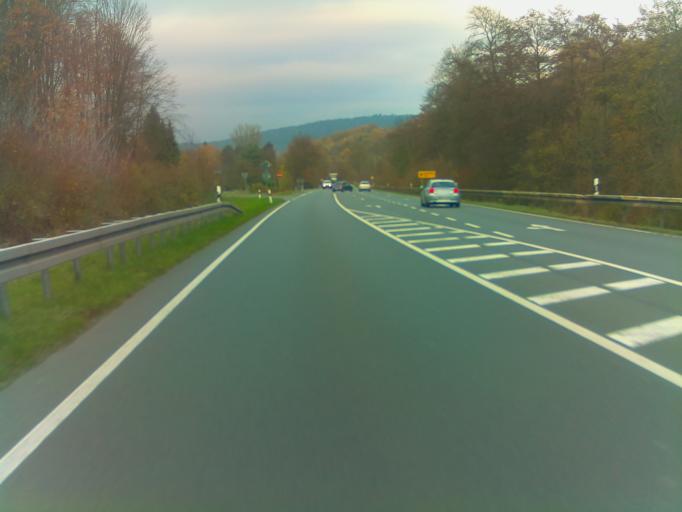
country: DE
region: Bavaria
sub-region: Regierungsbezirk Unterfranken
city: Weilbach
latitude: 49.6853
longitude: 9.2196
